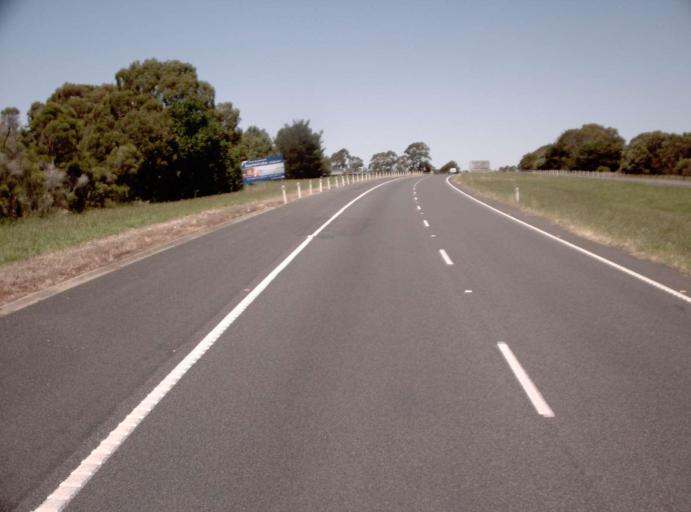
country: AU
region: Victoria
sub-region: Baw Baw
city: Warragul
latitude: -38.1386
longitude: 145.8835
